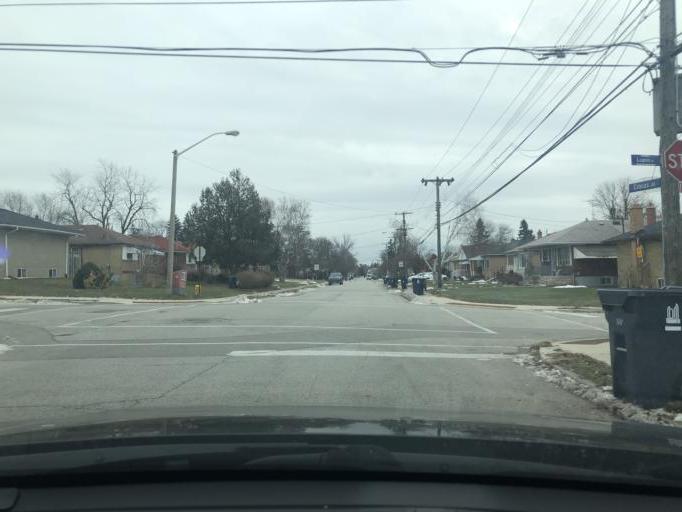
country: CA
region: Ontario
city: Scarborough
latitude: 43.7648
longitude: -79.3066
